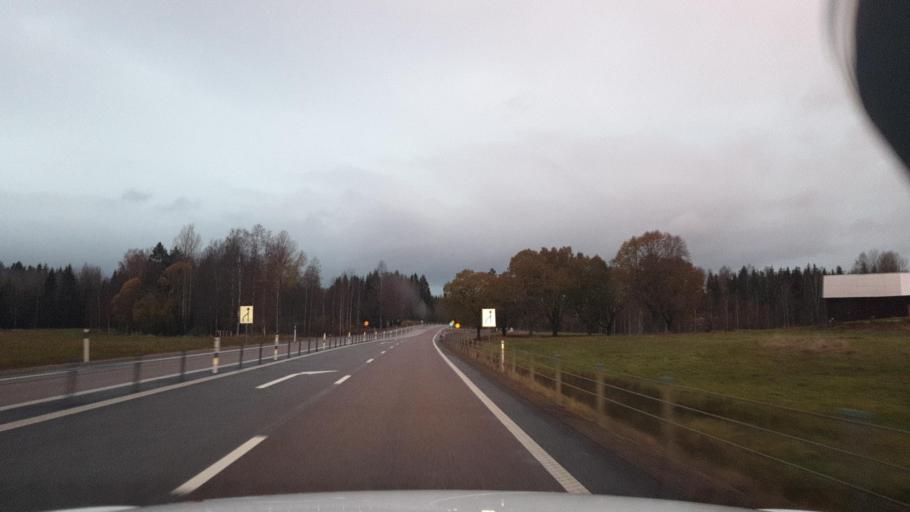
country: SE
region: Vaermland
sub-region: Eda Kommun
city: Amotfors
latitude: 59.7942
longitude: 12.3394
